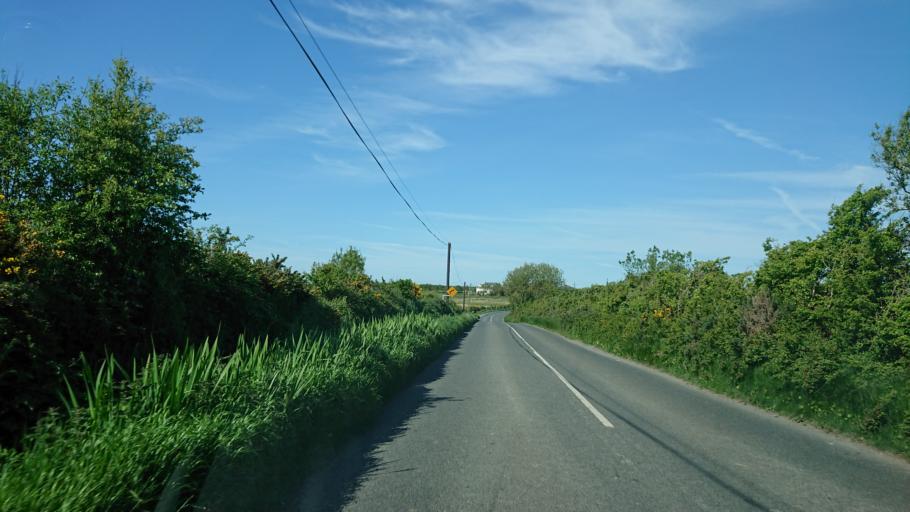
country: IE
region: Munster
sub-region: Waterford
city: Dunmore East
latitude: 52.1709
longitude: -7.0518
